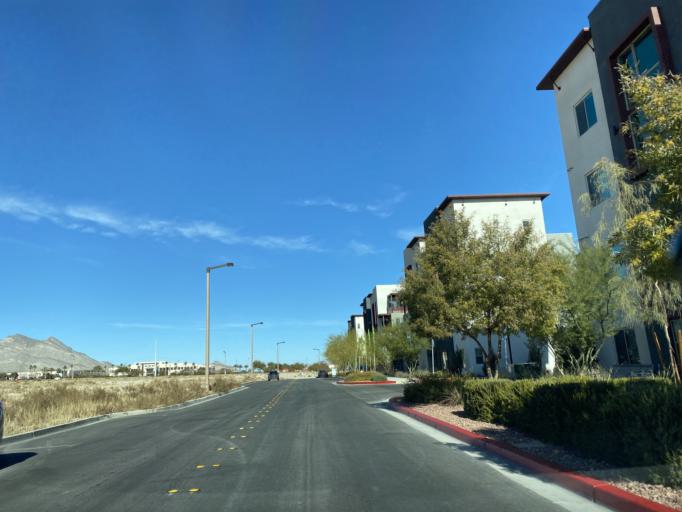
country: US
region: Nevada
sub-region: Clark County
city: Summerlin South
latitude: 36.1553
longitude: -115.3247
